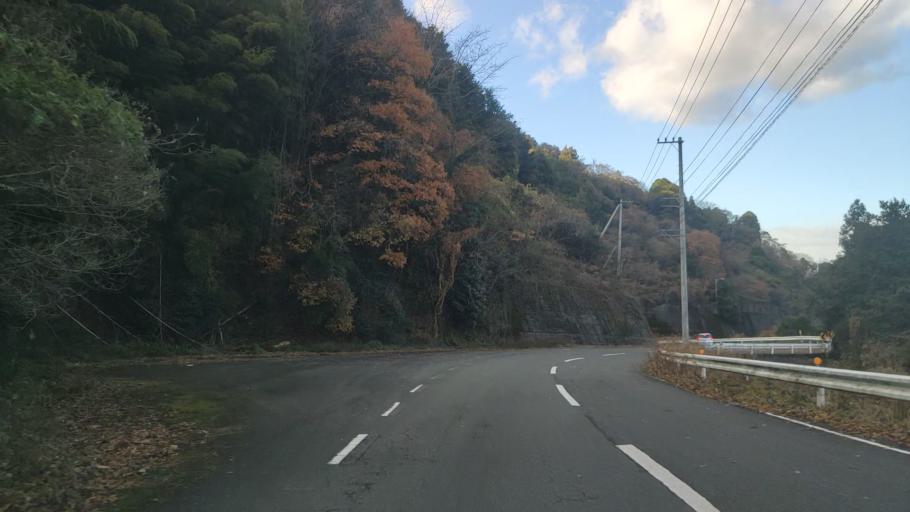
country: JP
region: Ehime
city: Saijo
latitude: 33.8804
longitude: 133.1330
